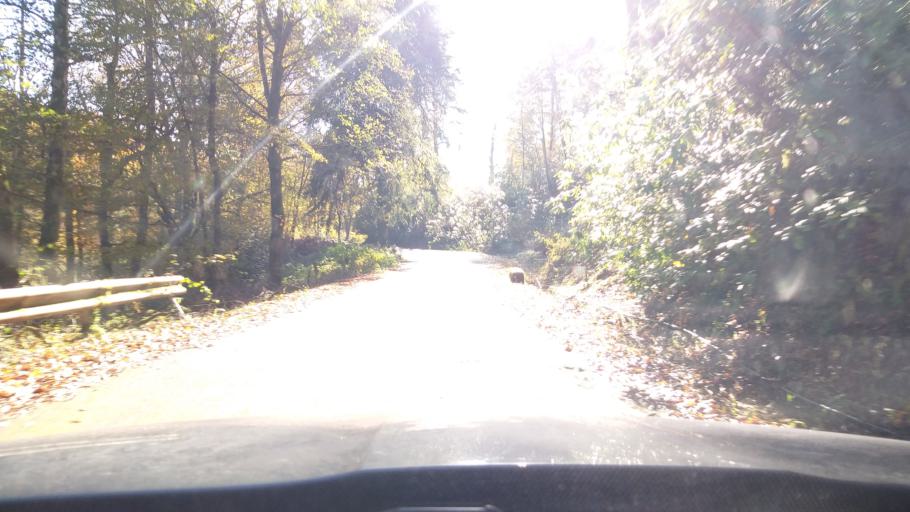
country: GE
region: Abkhazia
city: Bich'vinta
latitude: 43.1865
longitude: 40.4532
